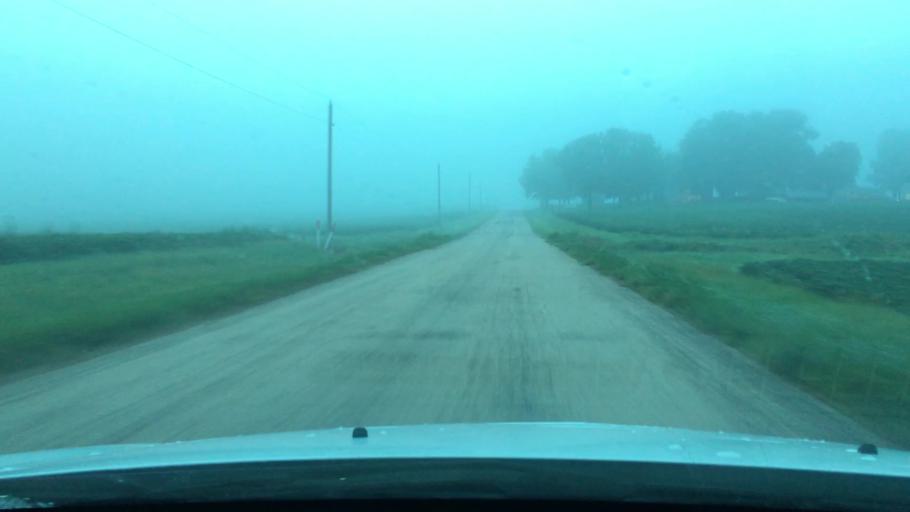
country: US
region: Illinois
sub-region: Ogle County
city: Rochelle
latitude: 41.9171
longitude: -88.9806
